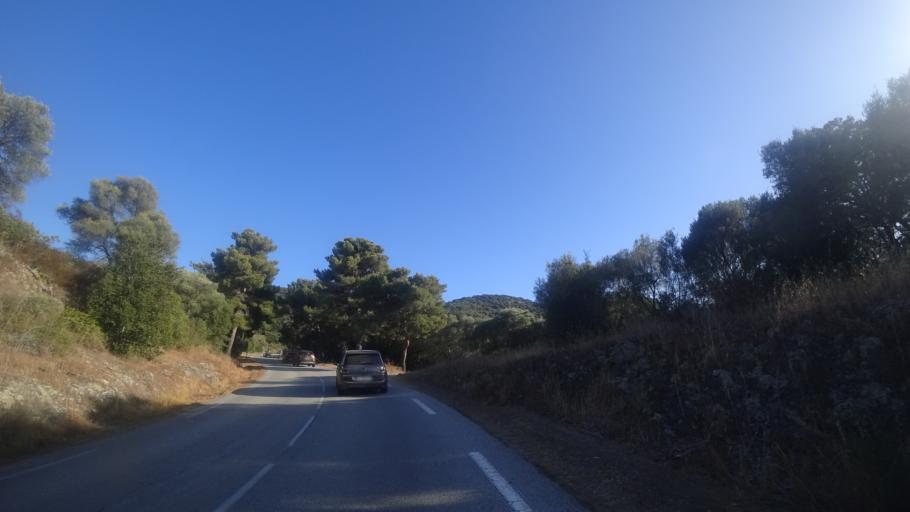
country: FR
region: Corsica
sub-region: Departement de la Corse-du-Sud
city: Cargese
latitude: 42.1721
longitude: 8.6083
